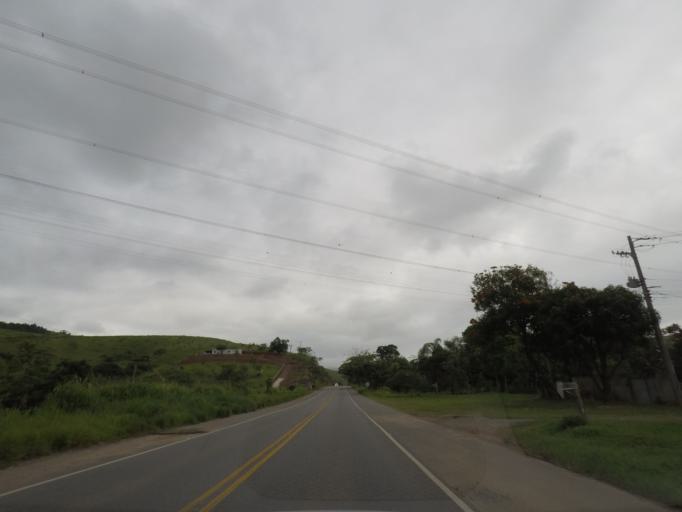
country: BR
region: Sao Paulo
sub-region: Guaratingueta
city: Guaratingueta
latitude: -22.8625
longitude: -45.1779
